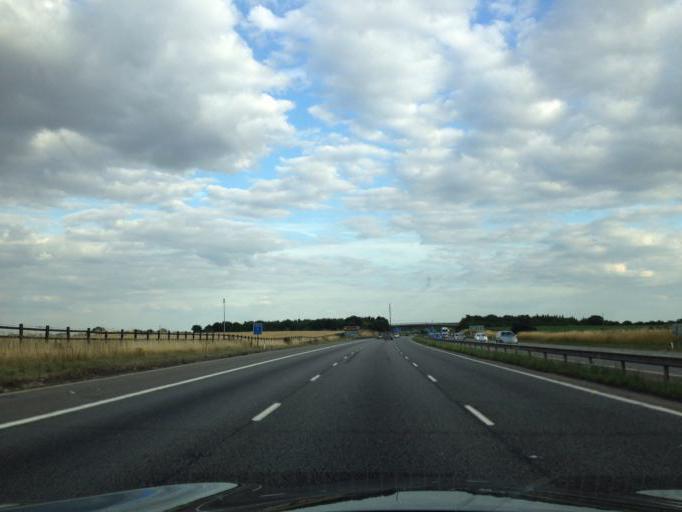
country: GB
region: England
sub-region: Oxfordshire
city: Somerton
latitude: 51.9608
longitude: -1.2197
